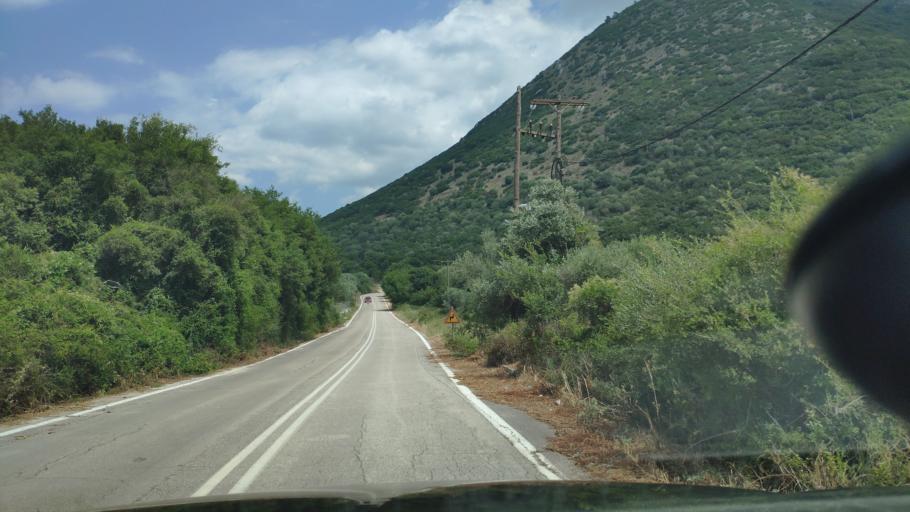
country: GR
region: Epirus
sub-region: Nomos Artas
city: Kampi
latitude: 39.2716
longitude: 20.9299
